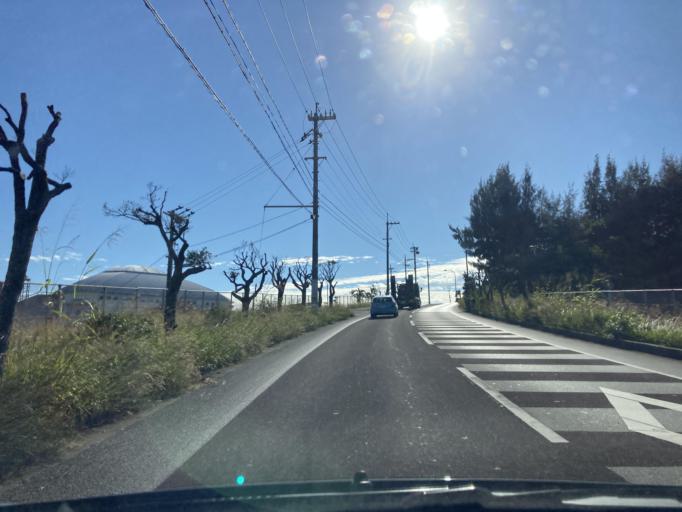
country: JP
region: Okinawa
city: Okinawa
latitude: 26.3699
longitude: 127.7708
